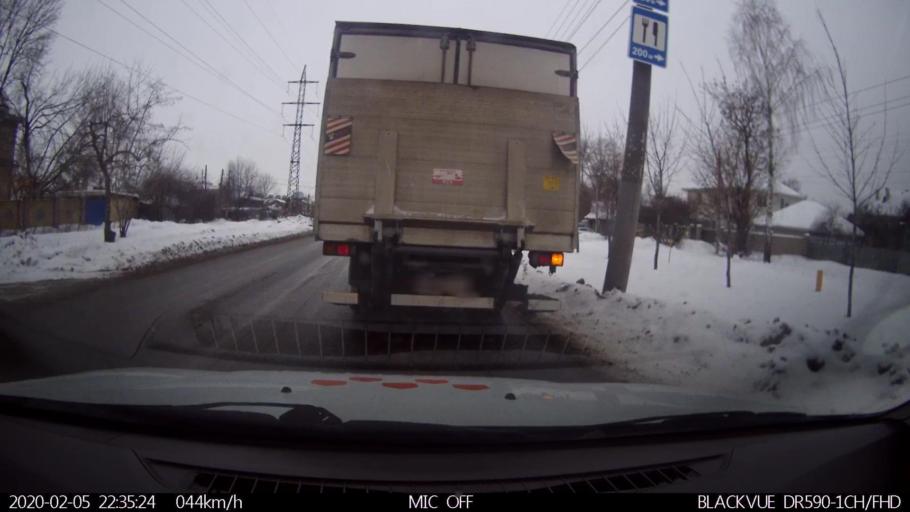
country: RU
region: Nizjnij Novgorod
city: Imeni Stepana Razina
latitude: 54.7345
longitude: 44.2403
